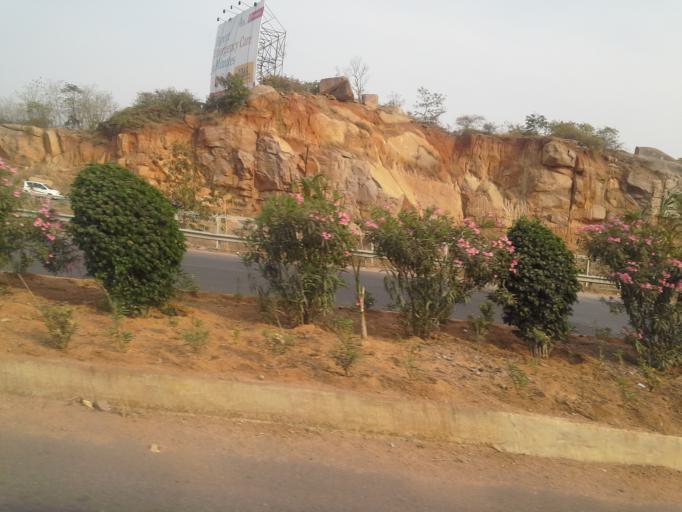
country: IN
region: Telangana
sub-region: Rangareddi
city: Kukatpalli
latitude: 17.4104
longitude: 78.3544
